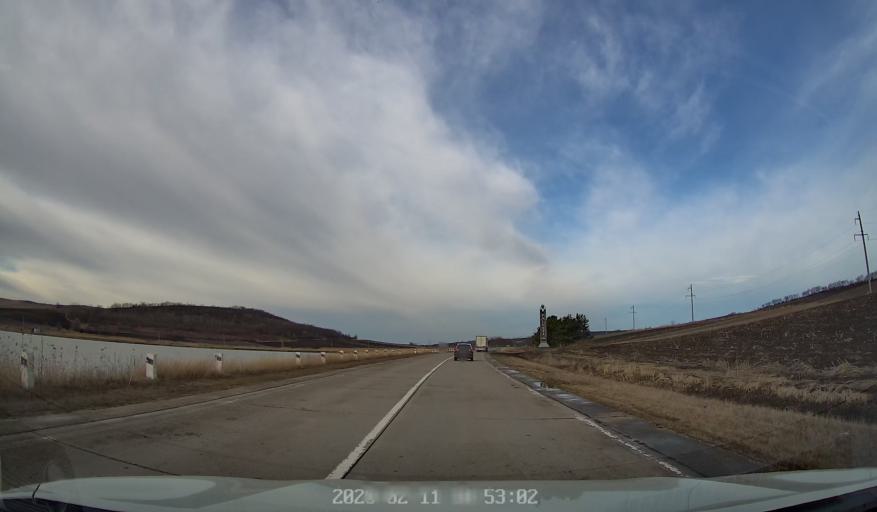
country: MD
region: Singerei
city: Bilicenii Vechi
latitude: 47.5821
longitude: 27.9503
